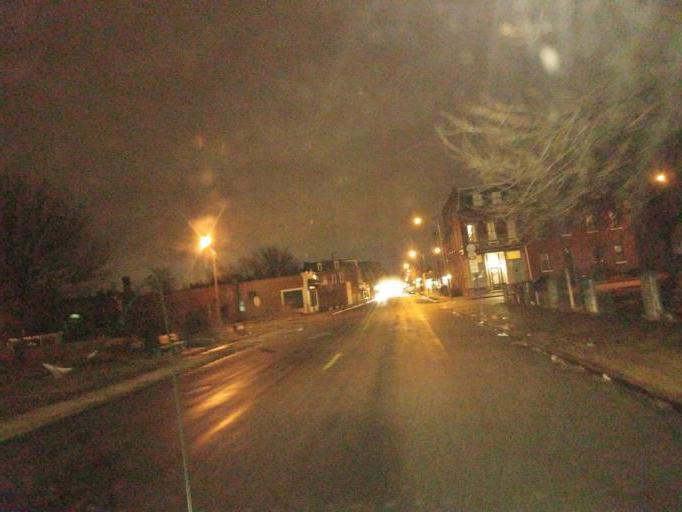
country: US
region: Missouri
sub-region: City of Saint Louis
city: St. Louis
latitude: 38.6507
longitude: -90.1994
